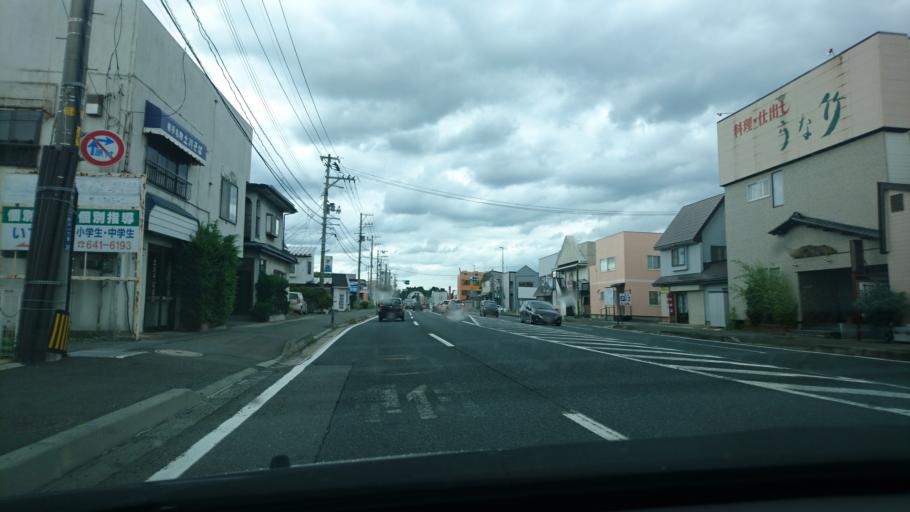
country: JP
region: Iwate
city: Morioka-shi
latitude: 39.7417
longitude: 141.1287
